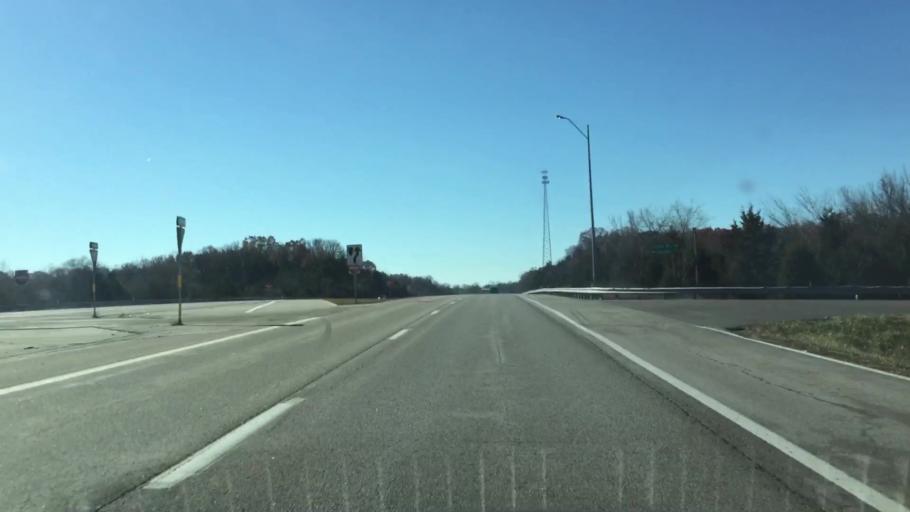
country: US
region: Missouri
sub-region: Cole County
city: Wardsville
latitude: 38.4847
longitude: -92.2722
